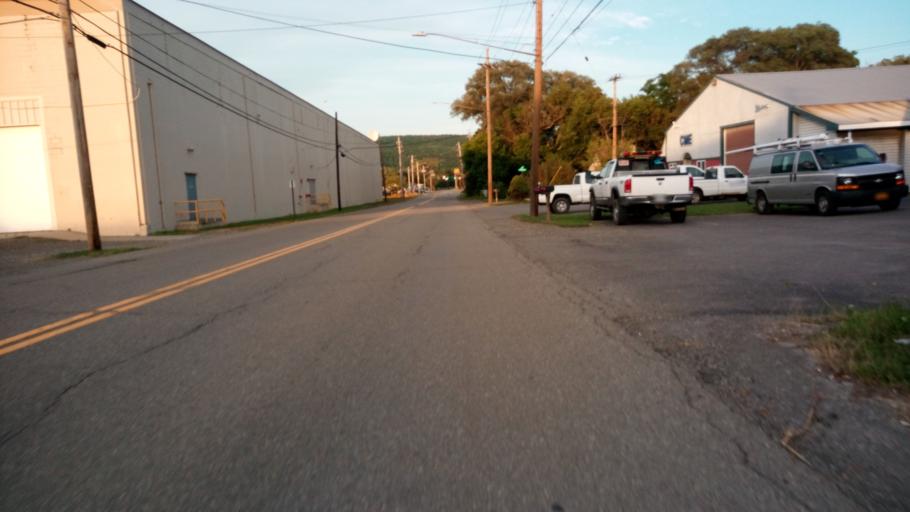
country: US
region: New York
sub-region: Chemung County
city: Horseheads
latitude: 42.1565
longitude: -76.8257
